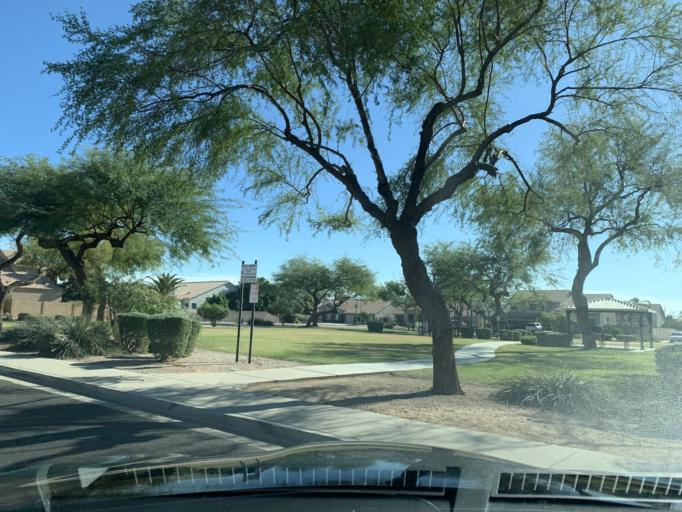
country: US
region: Arizona
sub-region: Pinal County
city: Apache Junction
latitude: 33.3834
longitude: -111.6268
